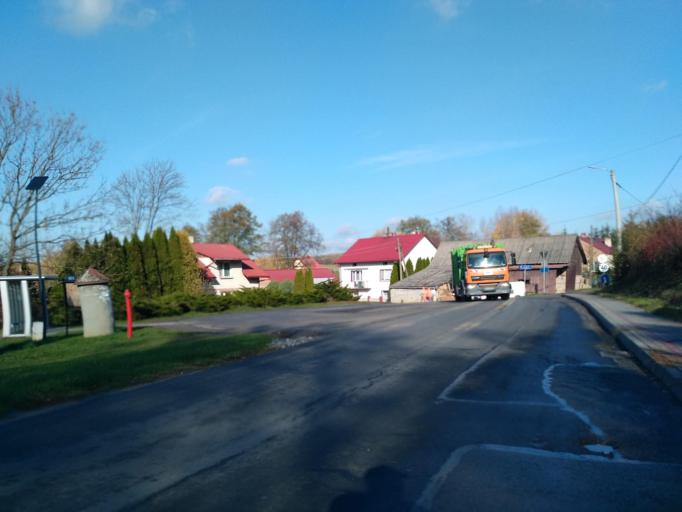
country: PL
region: Subcarpathian Voivodeship
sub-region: Powiat rzeszowski
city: Zglobien
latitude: 50.0299
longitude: 21.8613
